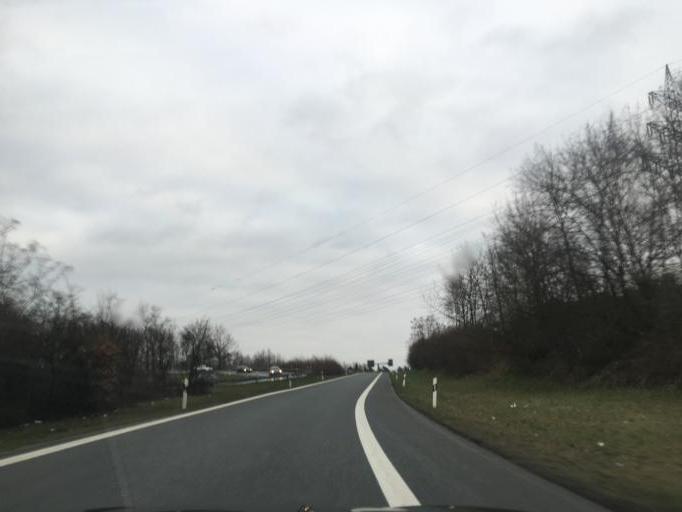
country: DE
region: Bavaria
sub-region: Regierungsbezirk Mittelfranken
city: Erlangen
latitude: 49.5593
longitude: 10.9894
